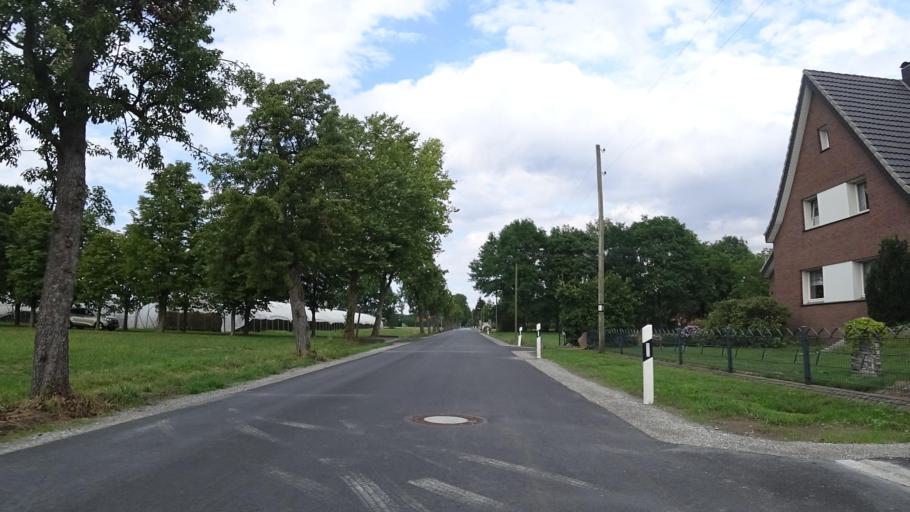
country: DE
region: North Rhine-Westphalia
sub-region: Regierungsbezirk Detmold
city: Steinhagen
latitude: 51.9603
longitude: 8.4294
